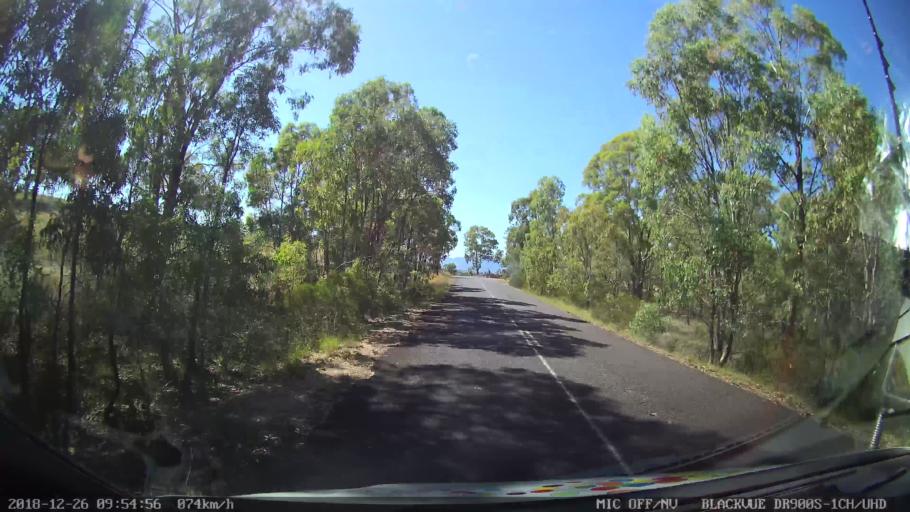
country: AU
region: New South Wales
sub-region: Mid-Western Regional
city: Kandos
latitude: -33.0350
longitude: 150.1624
